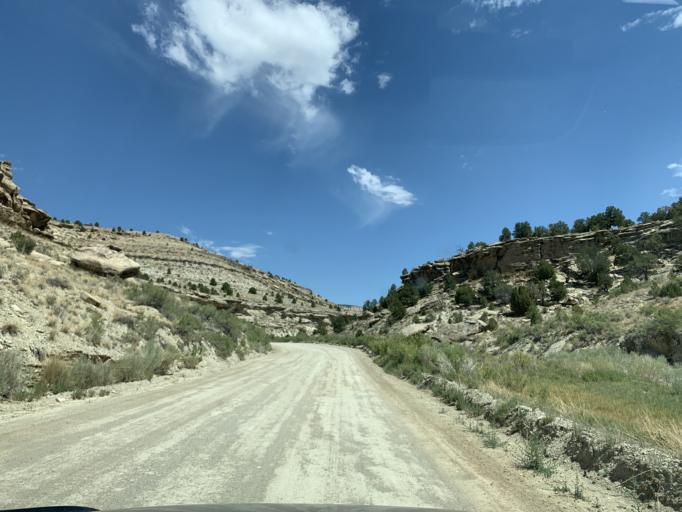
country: US
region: Utah
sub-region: Carbon County
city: East Carbon City
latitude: 39.8420
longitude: -110.2538
